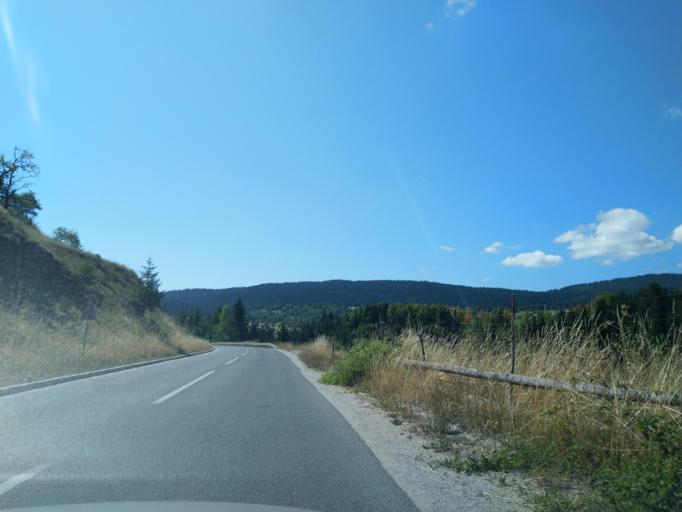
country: RS
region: Central Serbia
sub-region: Zlatiborski Okrug
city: Nova Varos
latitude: 43.4310
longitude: 19.8278
